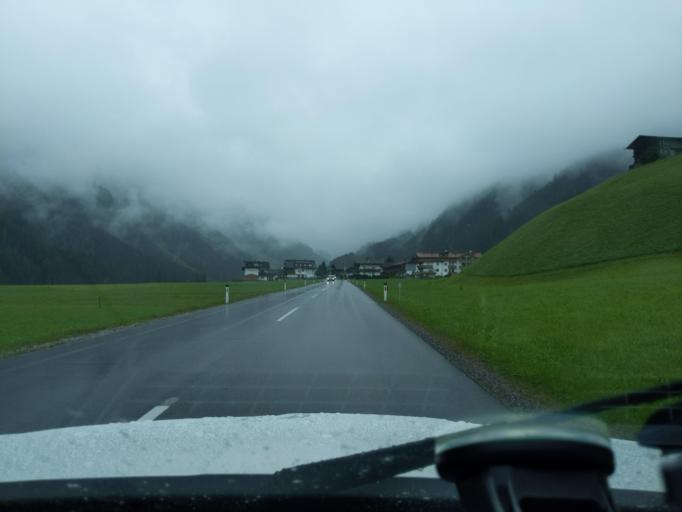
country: AT
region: Tyrol
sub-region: Politischer Bezirk Innsbruck Land
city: Schmirn
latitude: 47.1314
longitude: 11.7006
